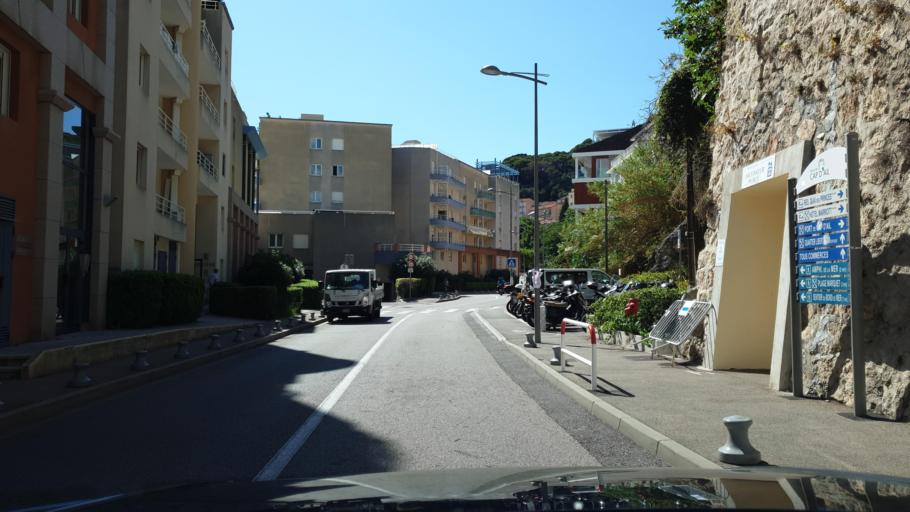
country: MC
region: Commune de Monaco
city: Fontvieille
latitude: 43.7263
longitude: 7.4127
